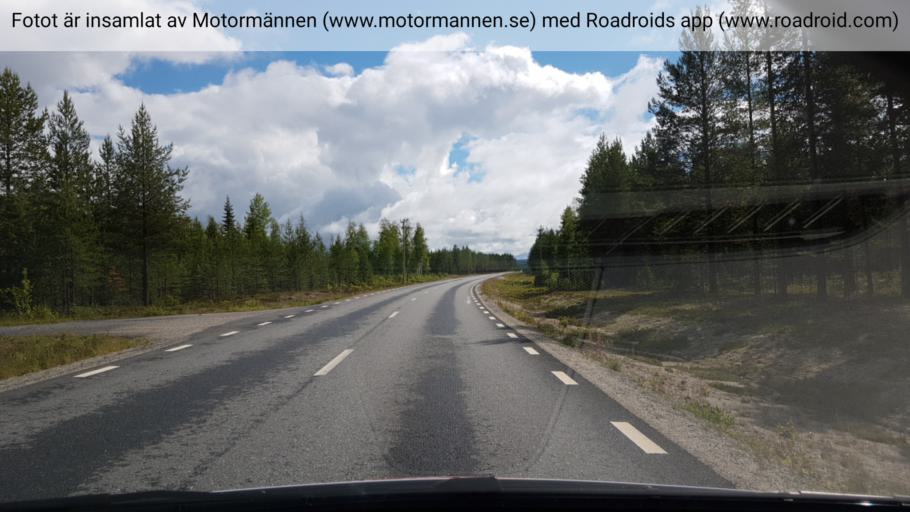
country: SE
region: Vaesterbotten
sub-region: Bjurholms Kommun
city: Bjurholm
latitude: 64.3159
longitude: 19.1601
